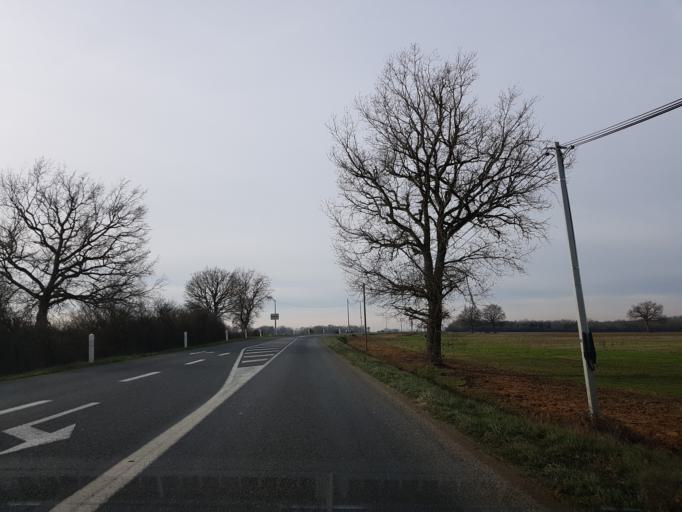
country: FR
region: Auvergne
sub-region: Departement de l'Allier
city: Yzeure
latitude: 46.5777
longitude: 3.4082
